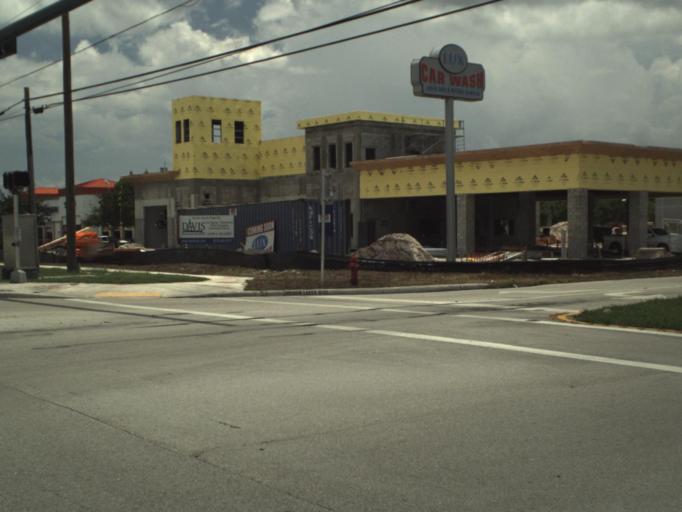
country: US
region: Florida
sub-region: Palm Beach County
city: Plantation Mobile Home Park
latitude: 26.7083
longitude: -80.1661
